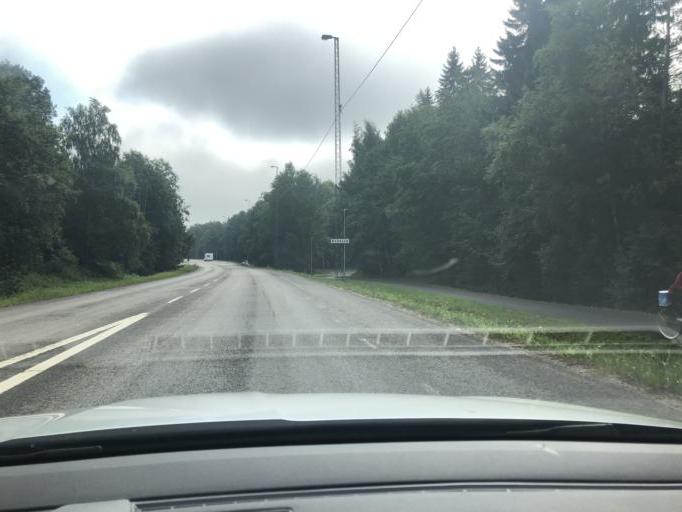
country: SE
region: Vaesternorrland
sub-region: Sundsvalls Kommun
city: Sundsvall
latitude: 62.4117
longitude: 17.3174
